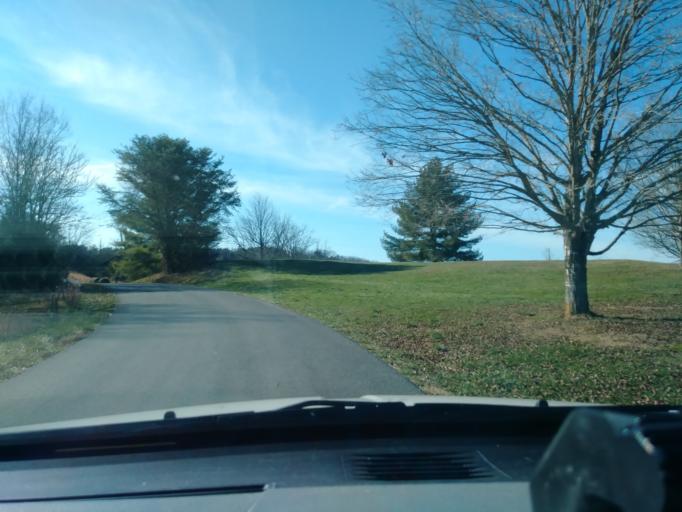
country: US
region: Tennessee
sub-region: Greene County
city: Greeneville
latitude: 36.0810
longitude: -82.8903
